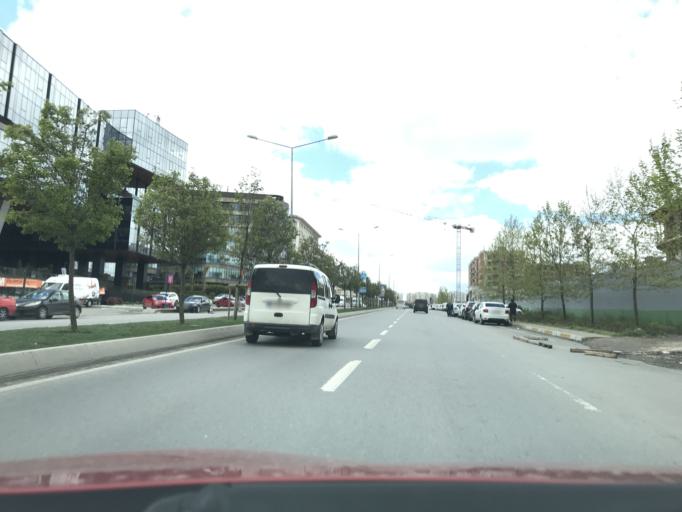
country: TR
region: Istanbul
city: Sultanbeyli
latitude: 40.9290
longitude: 29.3088
